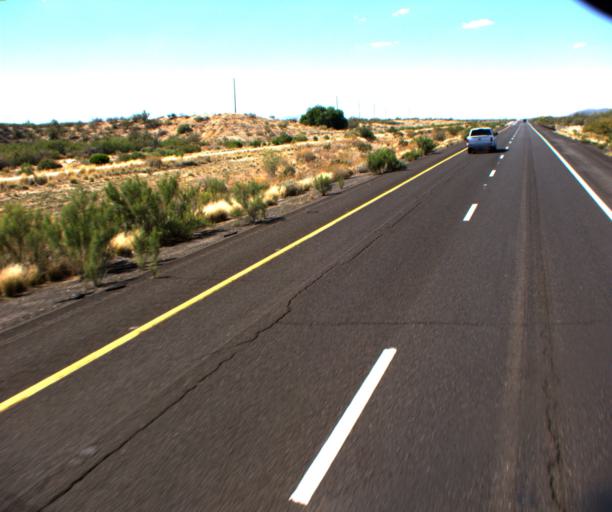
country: US
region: Arizona
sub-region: Yavapai County
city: Bagdad
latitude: 34.8437
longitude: -113.6353
